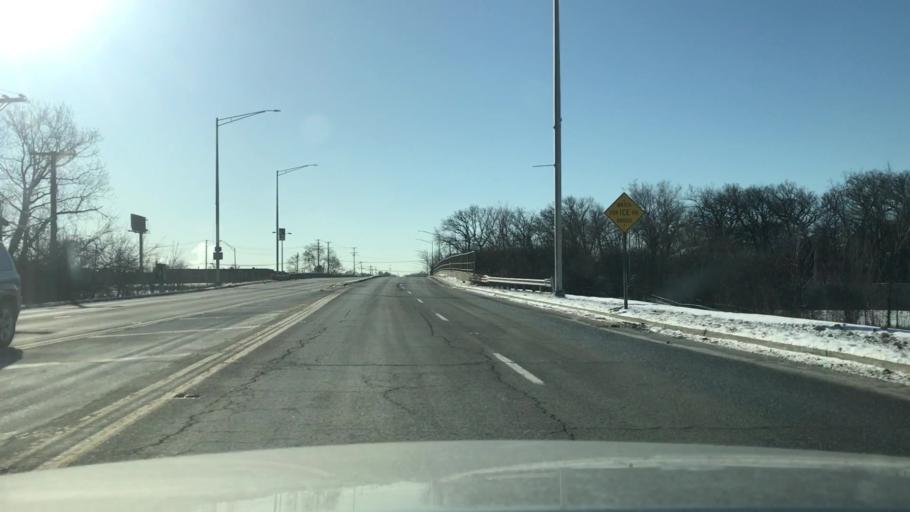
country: US
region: Illinois
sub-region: Cook County
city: Justice
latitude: 41.7461
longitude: -87.8386
